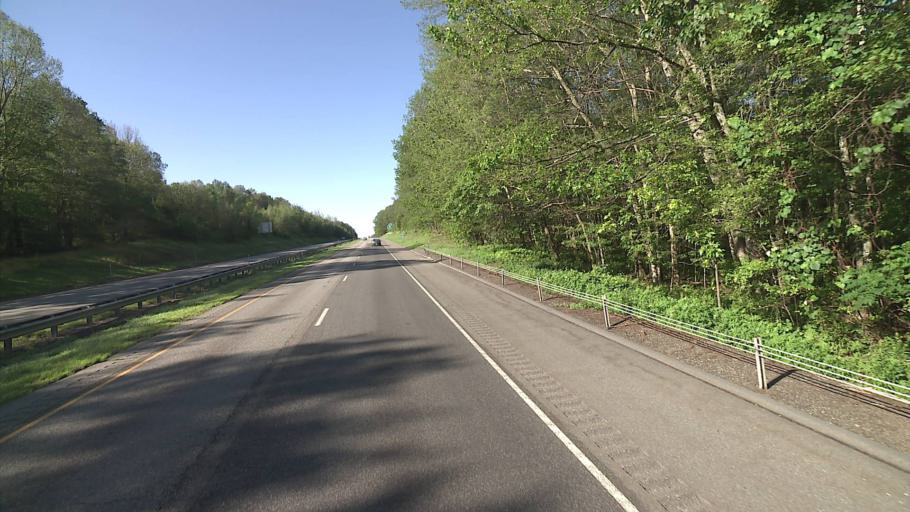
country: US
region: Connecticut
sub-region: Windham County
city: Moosup
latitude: 41.7045
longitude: -71.9002
